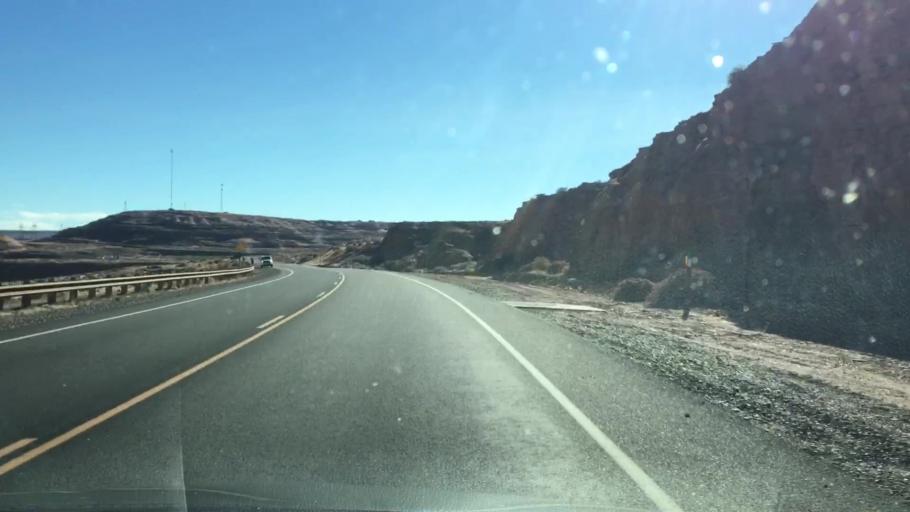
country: US
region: Arizona
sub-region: Coconino County
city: Page
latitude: 36.9495
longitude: -111.4937
